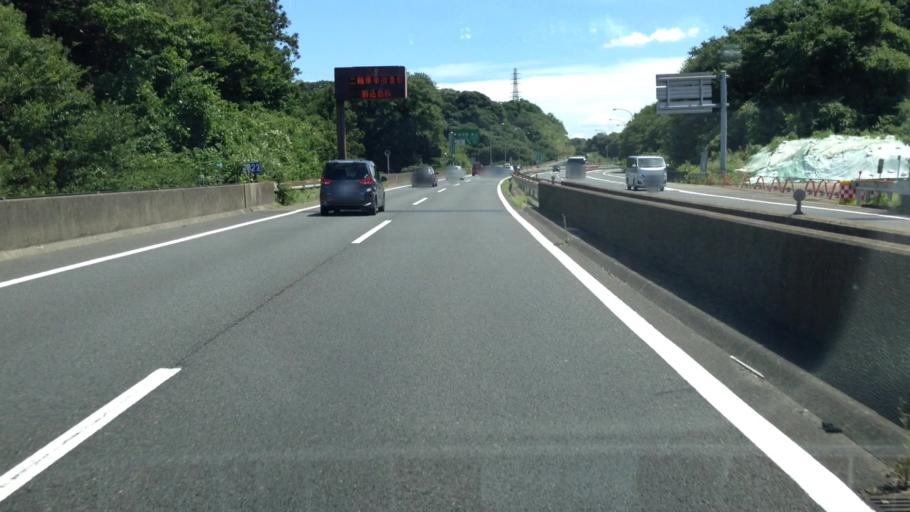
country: JP
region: Kanagawa
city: Yokosuka
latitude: 35.2808
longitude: 139.6301
